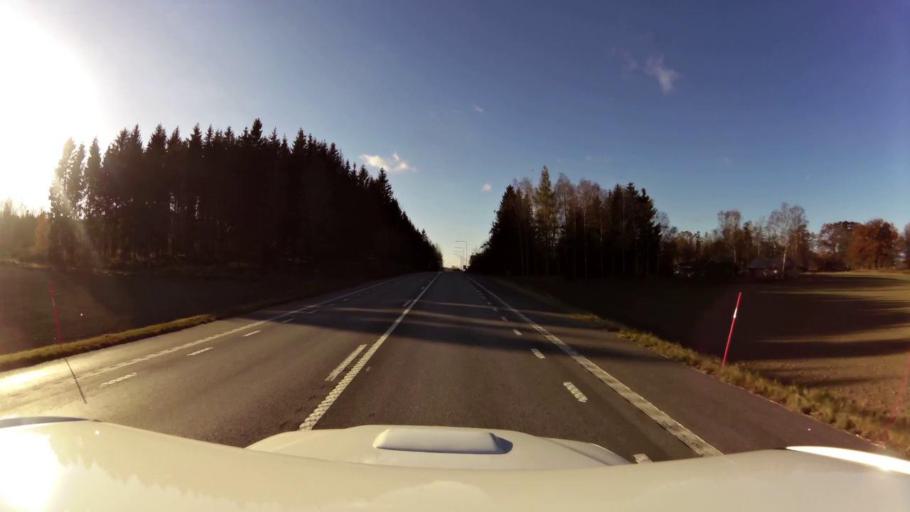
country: SE
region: OEstergoetland
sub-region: Linkopings Kommun
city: Linghem
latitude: 58.4415
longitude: 15.8083
